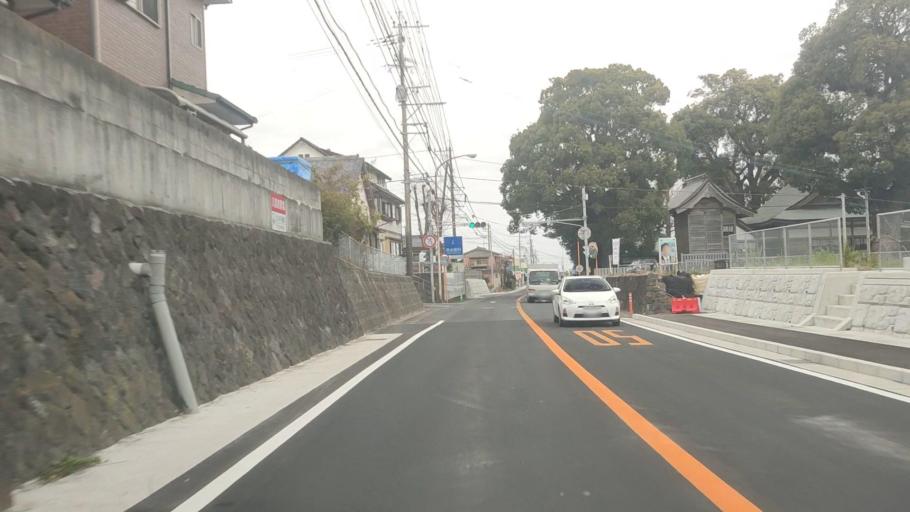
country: JP
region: Nagasaki
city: Shimabara
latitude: 32.8186
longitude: 130.3544
